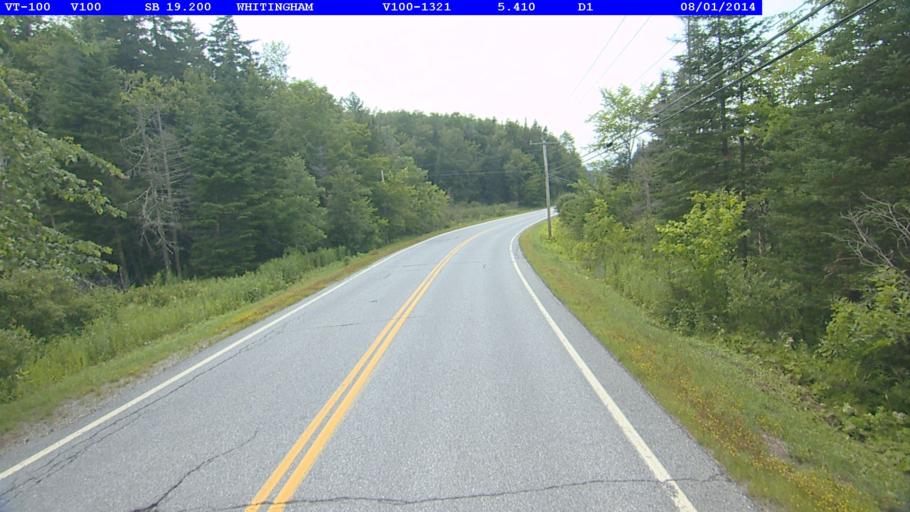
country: US
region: Massachusetts
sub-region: Franklin County
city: Charlemont
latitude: 42.7869
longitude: -72.8602
